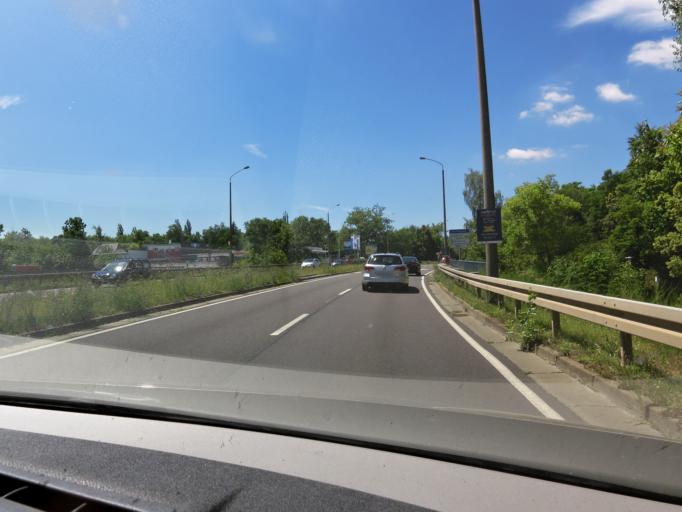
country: DE
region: Saxony-Anhalt
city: Merseburg
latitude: 51.3519
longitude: 11.9997
